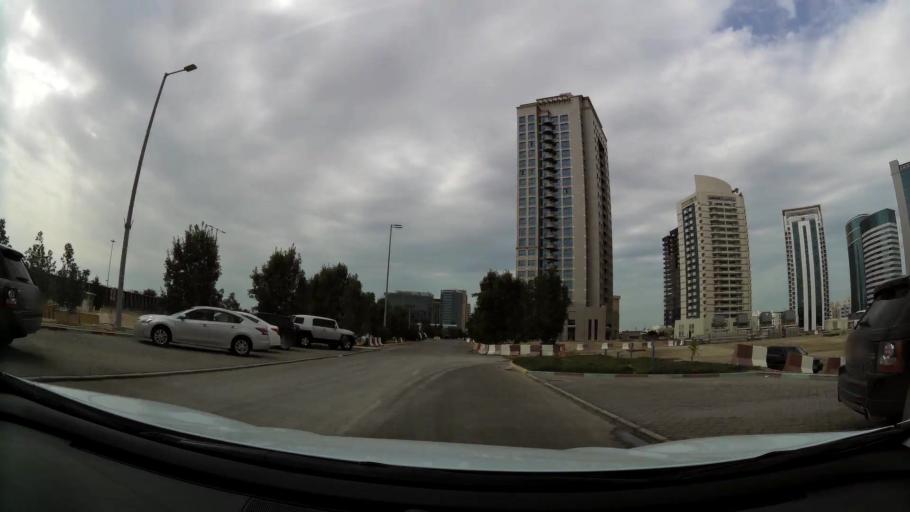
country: AE
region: Abu Dhabi
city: Abu Dhabi
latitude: 24.4291
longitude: 54.4355
